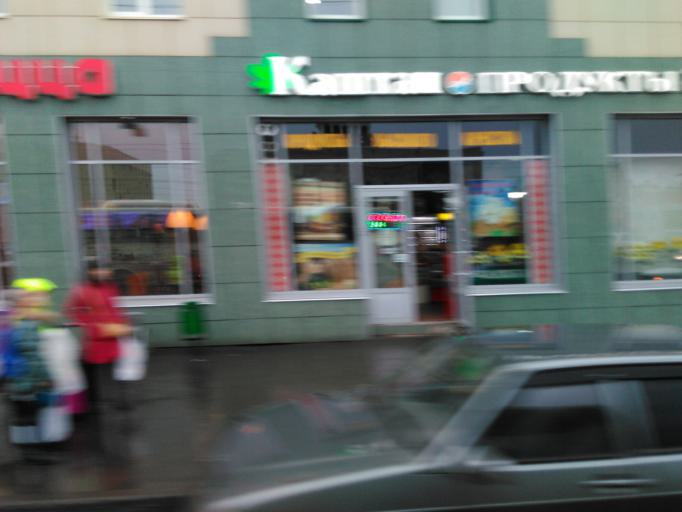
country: RU
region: Tatarstan
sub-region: Gorod Kazan'
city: Kazan
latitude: 55.7896
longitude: 49.1015
